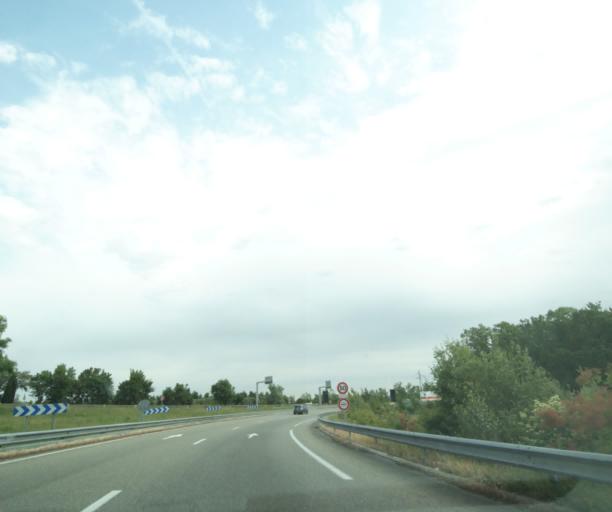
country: FR
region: Midi-Pyrenees
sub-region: Departement du Tarn-et-Garonne
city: Campsas
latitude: 43.9274
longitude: 1.3110
